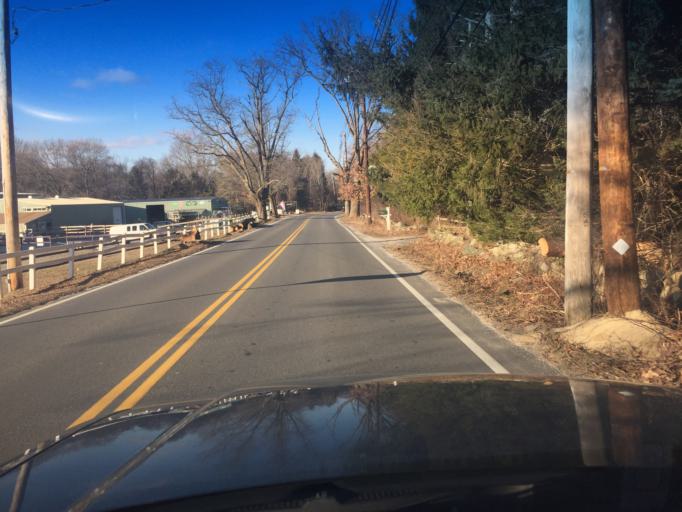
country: US
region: Massachusetts
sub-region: Middlesex County
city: Sherborn
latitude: 42.2656
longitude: -71.3802
